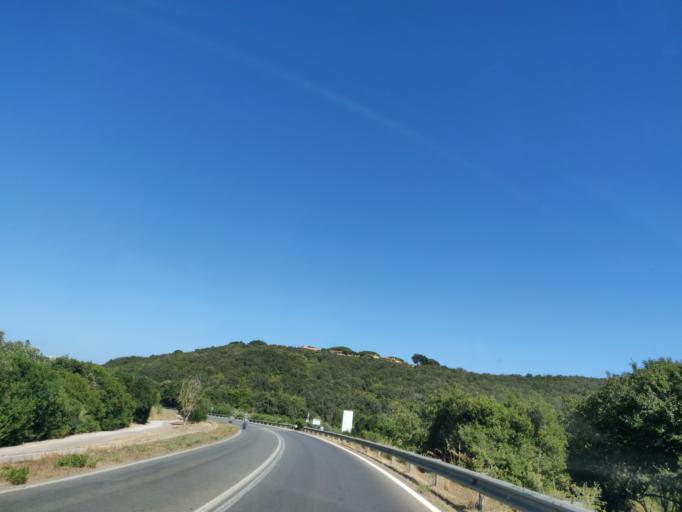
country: IT
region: Tuscany
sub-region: Provincia di Grosseto
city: Porto Ercole
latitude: 42.4296
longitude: 11.1672
